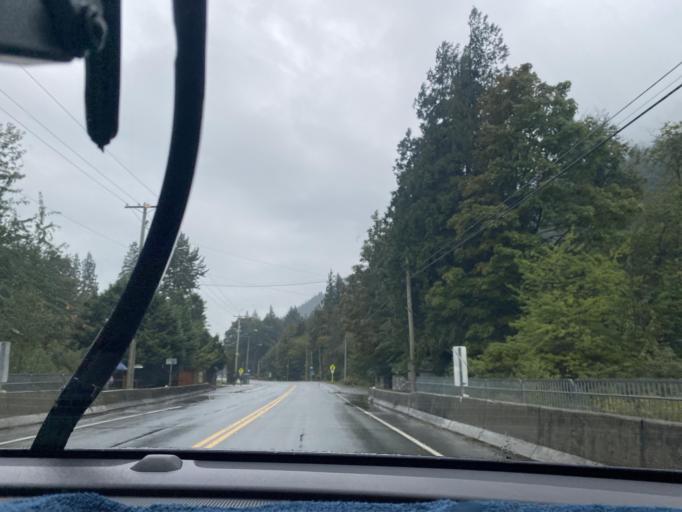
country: CA
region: British Columbia
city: Agassiz
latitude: 49.3010
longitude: -121.7854
